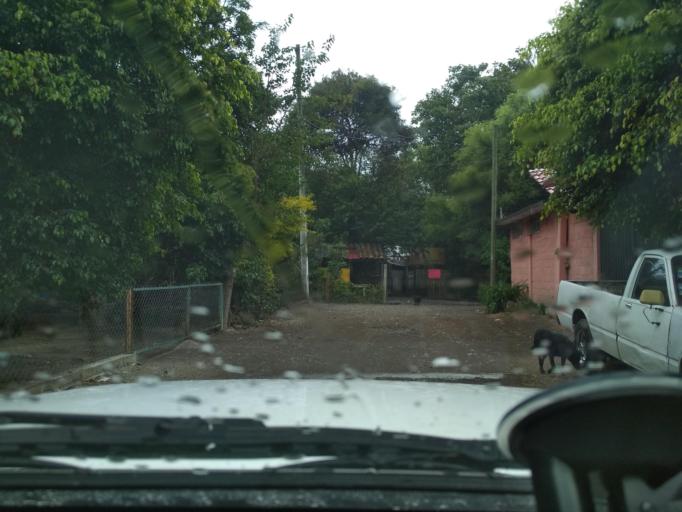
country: MX
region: Veracruz
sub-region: Nogales
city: Taza de Agua Ojo Zarco
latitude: 18.7802
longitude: -97.2051
